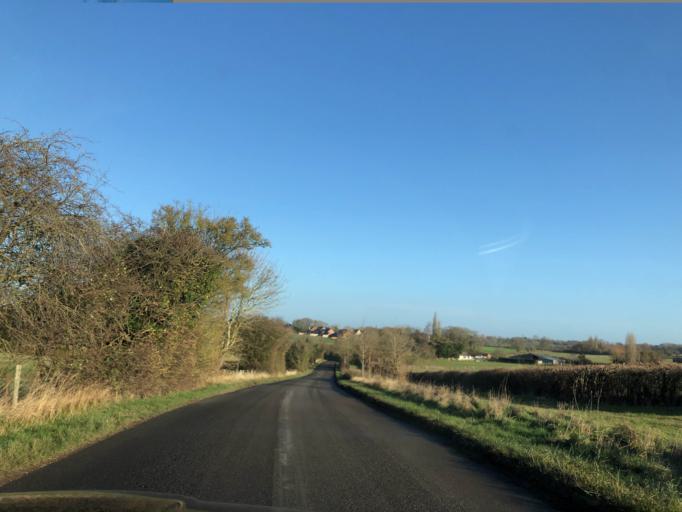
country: GB
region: England
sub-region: Warwickshire
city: Wellesbourne Mountford
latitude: 52.1936
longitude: -1.5138
